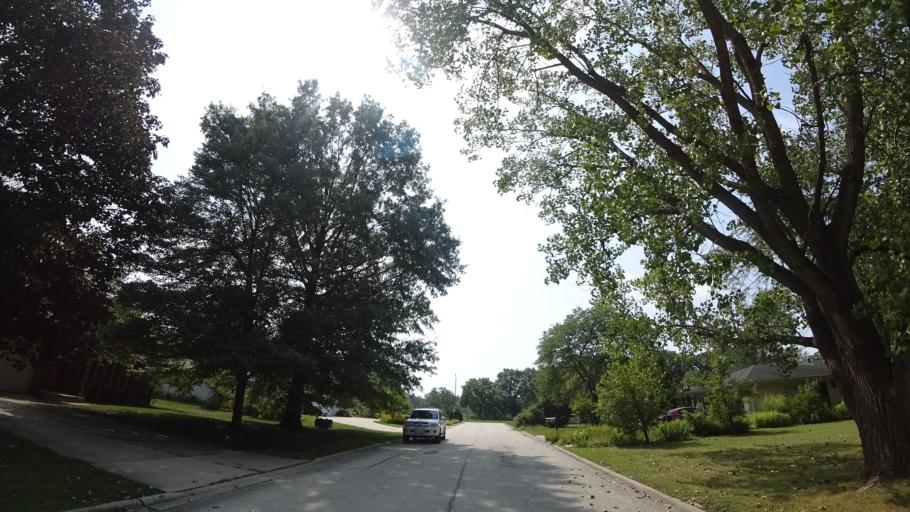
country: US
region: Illinois
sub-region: Cook County
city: Orland Park
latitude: 41.6236
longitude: -87.8687
